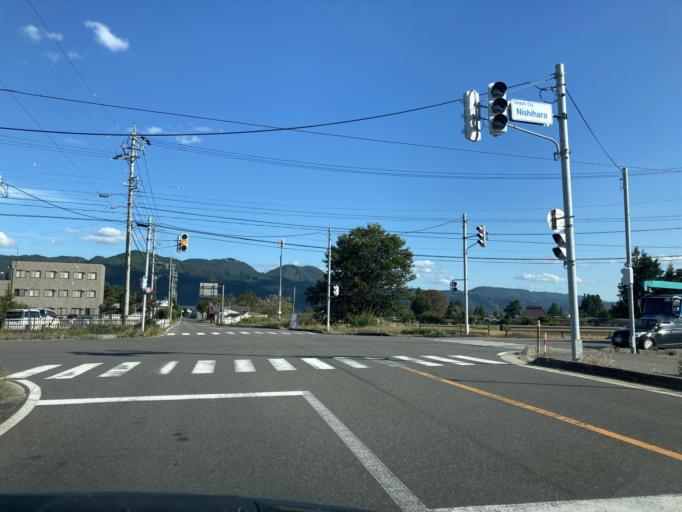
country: JP
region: Nagano
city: Omachi
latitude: 36.5239
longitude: 137.8338
